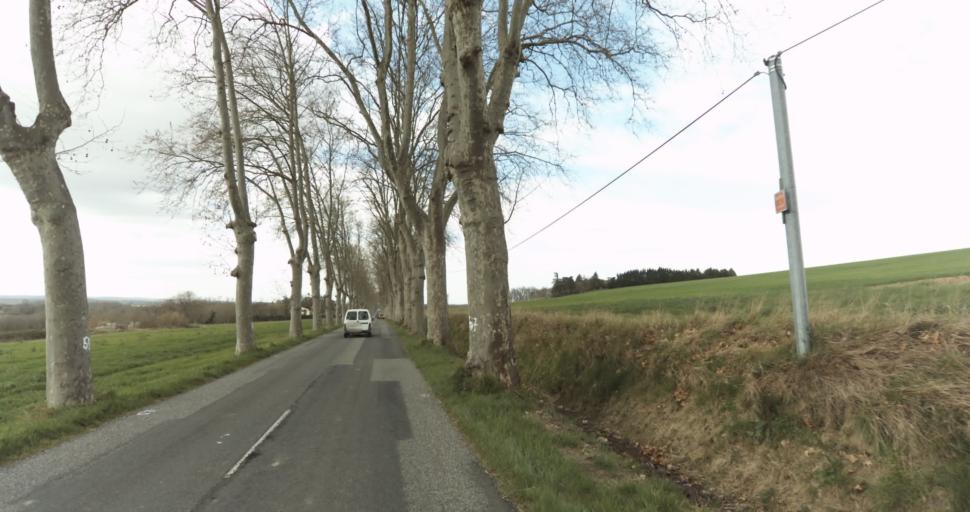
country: FR
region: Midi-Pyrenees
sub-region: Departement de la Haute-Garonne
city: Auterive
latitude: 43.3685
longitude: 1.4724
